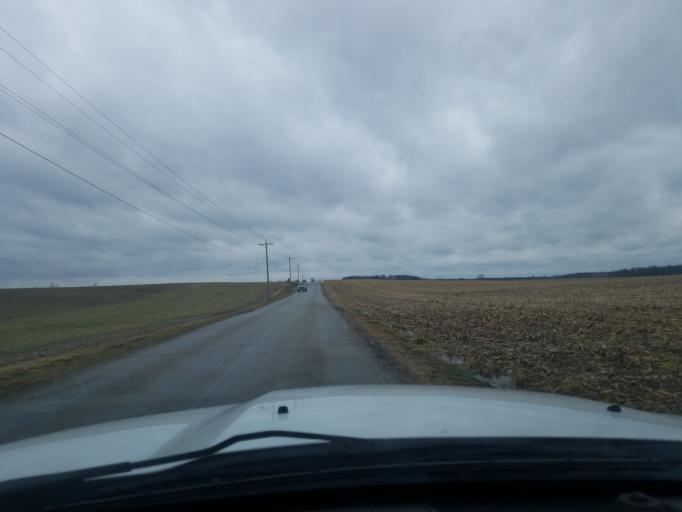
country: US
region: Indiana
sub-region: Noble County
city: Albion
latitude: 41.4353
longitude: -85.3947
